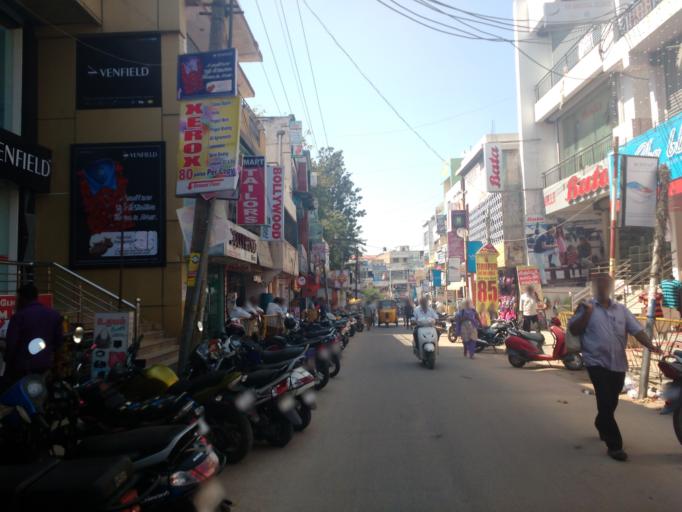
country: IN
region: Tamil Nadu
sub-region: Krishnagiri
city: Hosur
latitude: 12.7334
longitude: 77.8271
